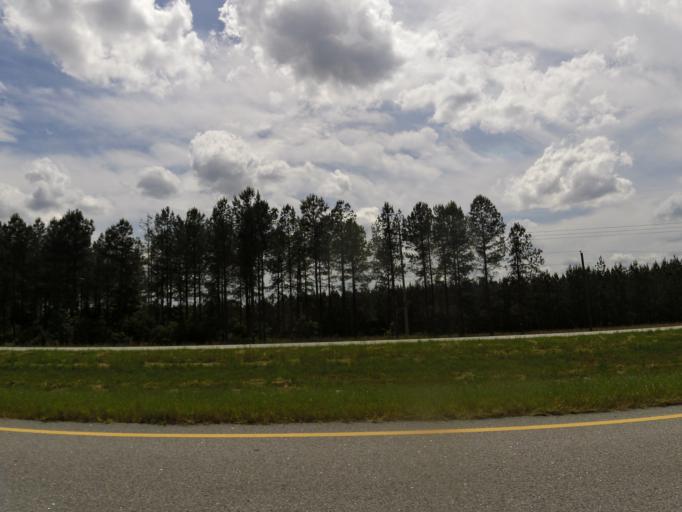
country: US
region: Georgia
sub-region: Jefferson County
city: Wadley
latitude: 32.7840
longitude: -82.3927
